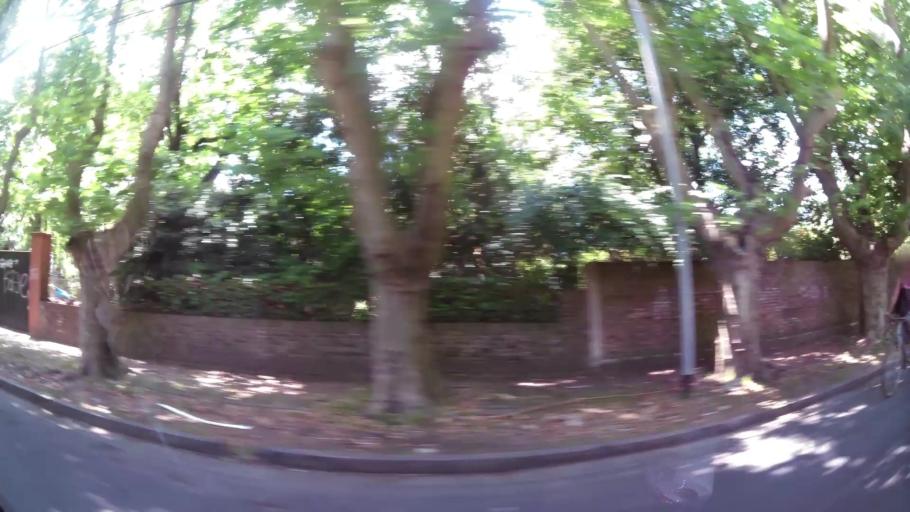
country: AR
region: Buenos Aires
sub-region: Partido de Tigre
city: Tigre
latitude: -34.4160
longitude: -58.5900
